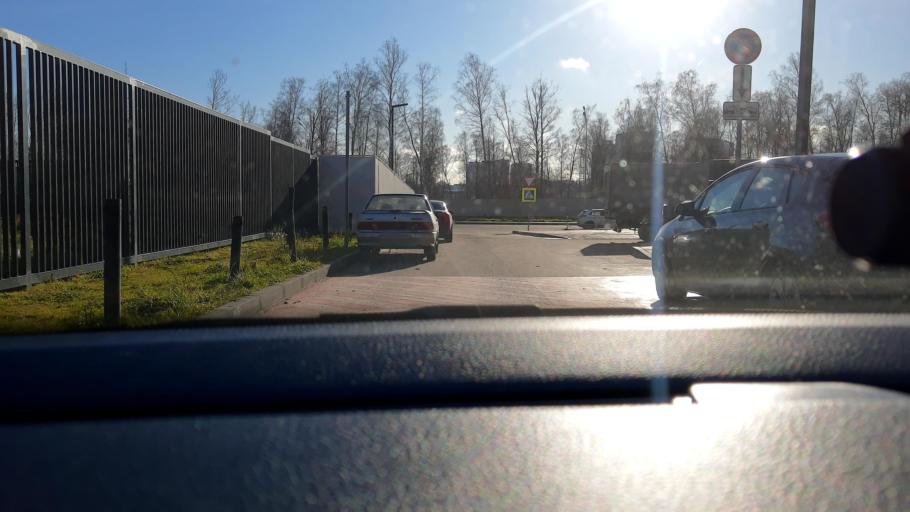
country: RU
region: Moscow
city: Ivanovskoye
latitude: 55.7841
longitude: 37.8487
